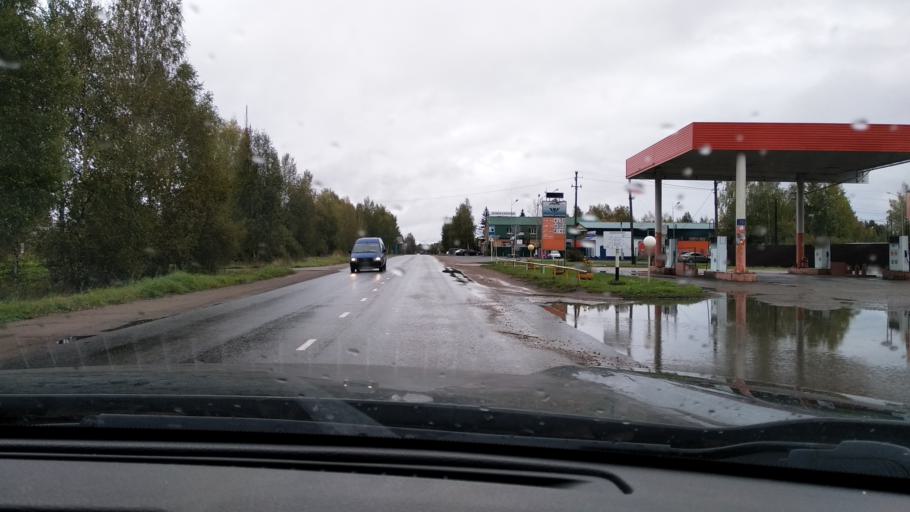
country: RU
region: Tverskaya
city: Kashin
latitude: 57.3583
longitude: 37.5795
